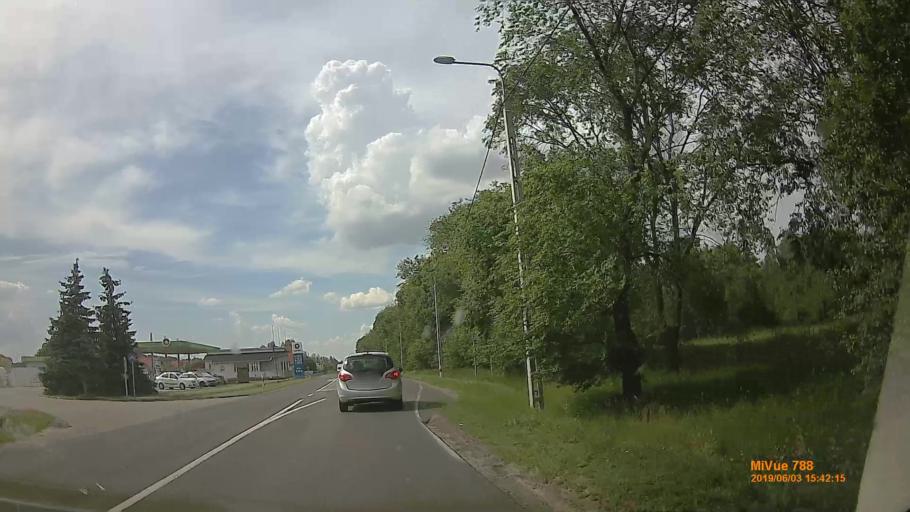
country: HU
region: Bacs-Kiskun
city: Kiskoros
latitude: 46.6302
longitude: 19.2689
